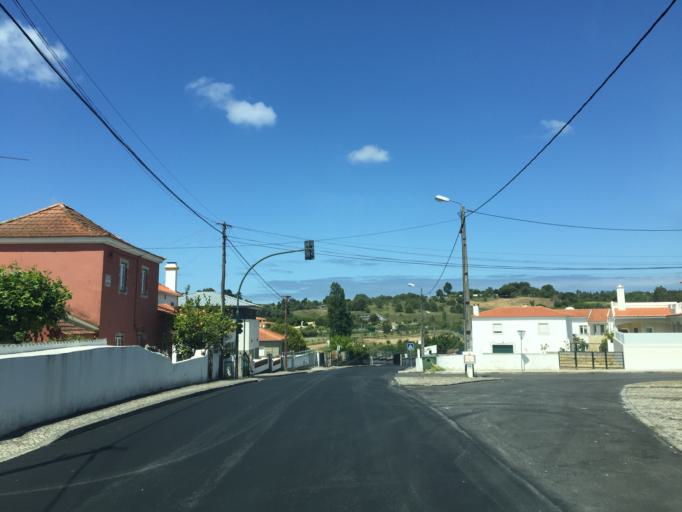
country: PT
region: Lisbon
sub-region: Sintra
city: Sintra
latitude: 38.8073
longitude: -9.3992
